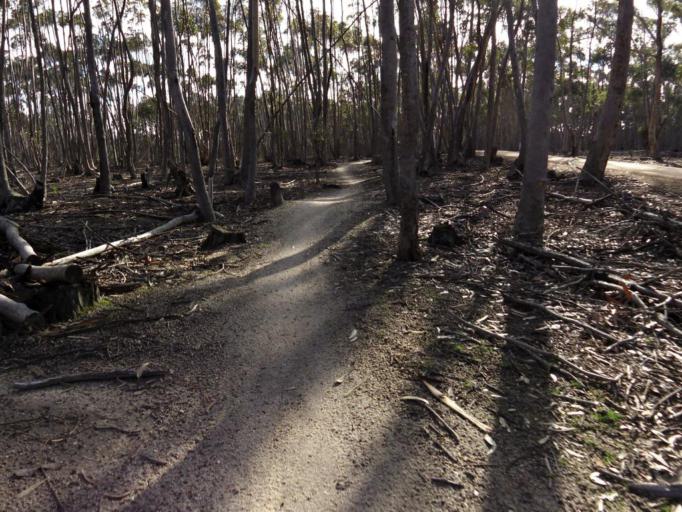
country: AU
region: Victoria
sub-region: Greater Geelong
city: Lara
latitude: -37.9416
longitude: 144.4114
